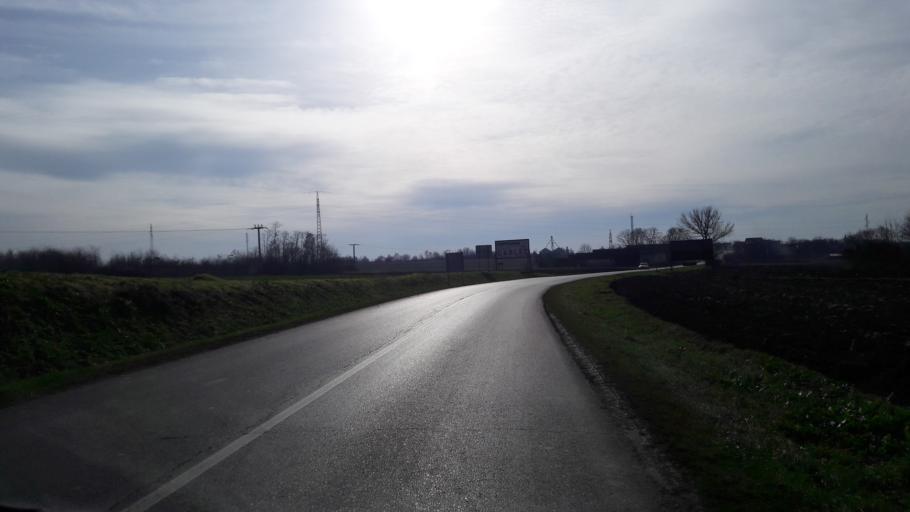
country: HR
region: Vukovarsko-Srijemska
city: Vodinci
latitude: 45.2968
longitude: 18.5608
